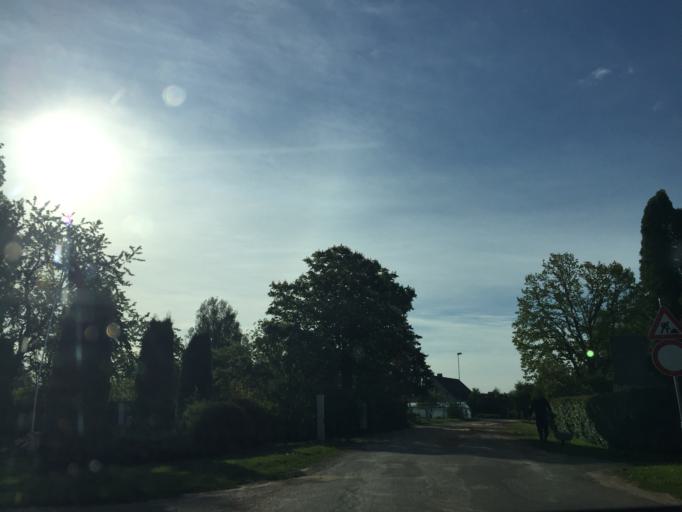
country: LV
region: Lecava
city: Iecava
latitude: 56.6019
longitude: 24.2104
